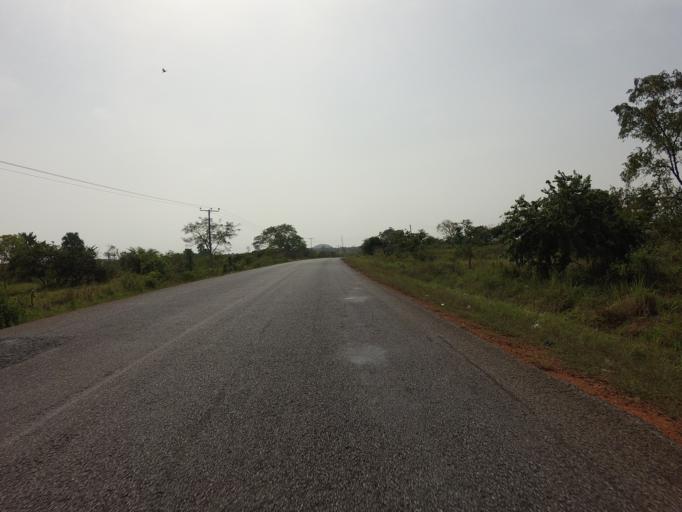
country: GH
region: Volta
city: Ho
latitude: 6.3896
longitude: 0.1836
